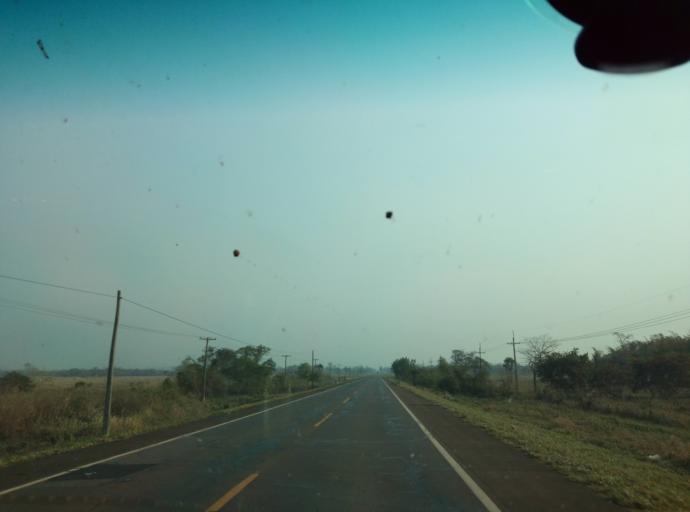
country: PY
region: Caaguazu
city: Carayao
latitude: -25.1285
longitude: -56.3527
